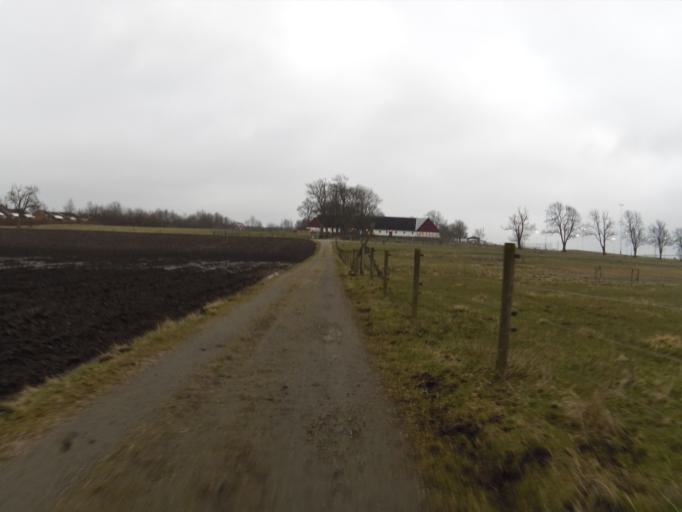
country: SE
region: Skane
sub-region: Lunds Kommun
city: Lund
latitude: 55.7311
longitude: 13.1542
